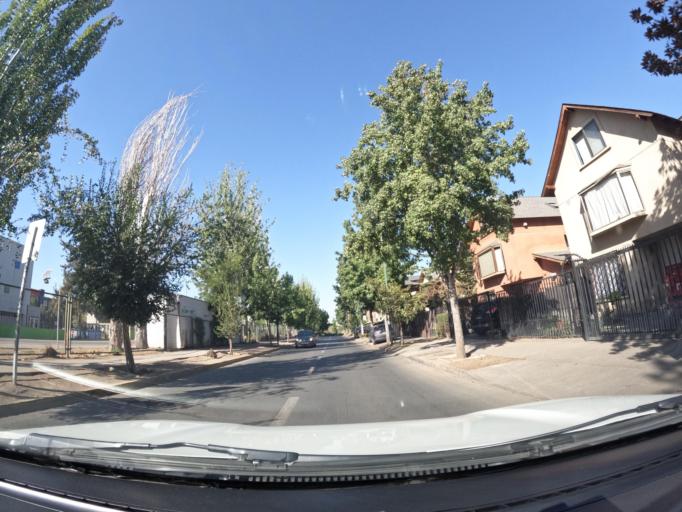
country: CL
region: Santiago Metropolitan
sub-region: Provincia de Santiago
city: Villa Presidente Frei, Nunoa, Santiago, Chile
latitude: -33.4918
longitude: -70.5772
